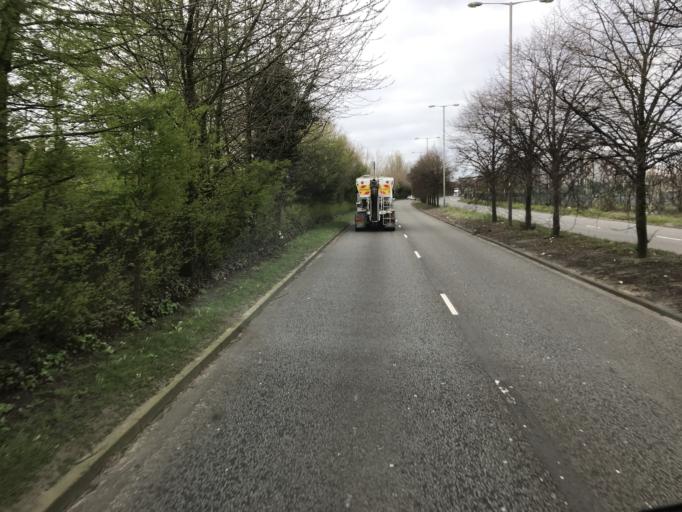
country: GB
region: England
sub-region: Borough of Halton
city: Hale
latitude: 53.3471
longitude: -2.8270
